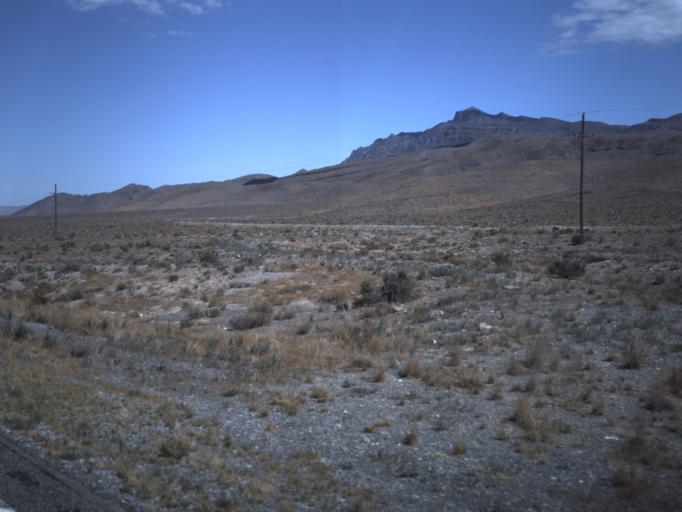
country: US
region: Utah
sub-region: Beaver County
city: Milford
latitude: 39.0311
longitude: -113.3829
